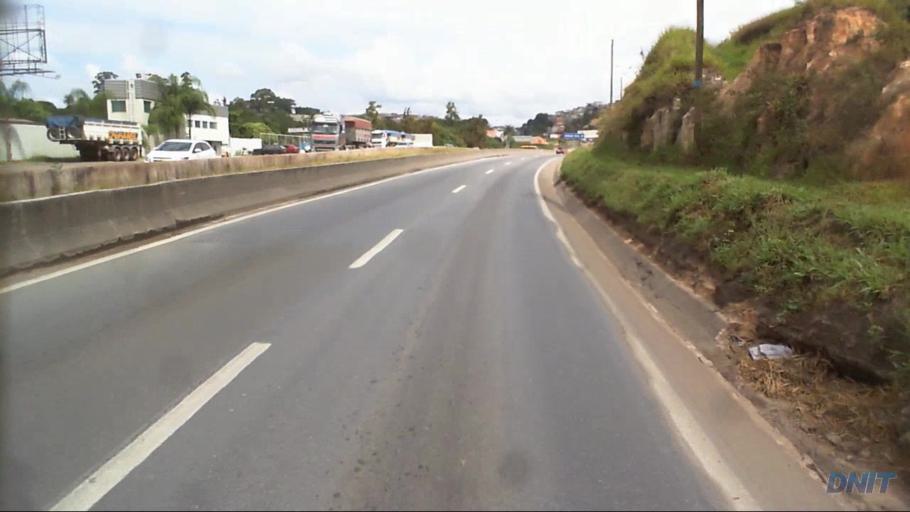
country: BR
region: Minas Gerais
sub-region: Santa Luzia
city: Santa Luzia
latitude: -19.8422
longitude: -43.8855
